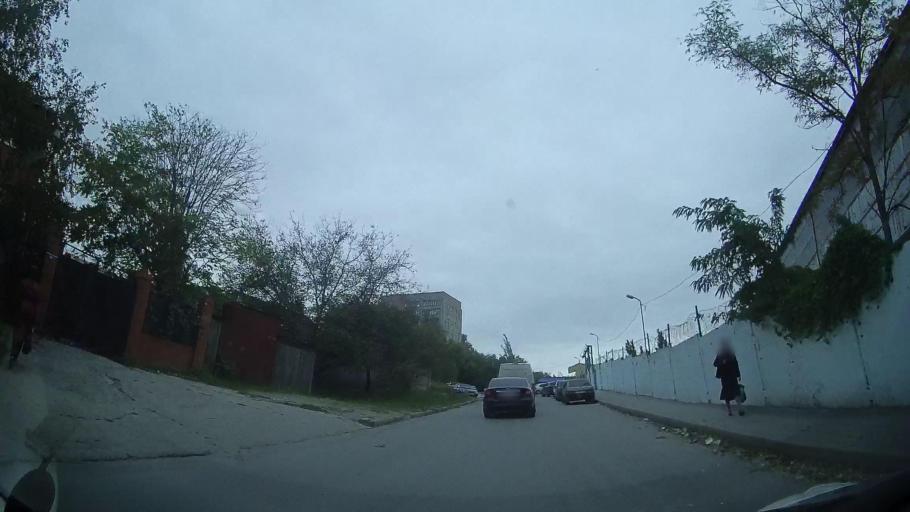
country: RU
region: Rostov
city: Severnyy
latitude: 47.2687
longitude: 39.6817
